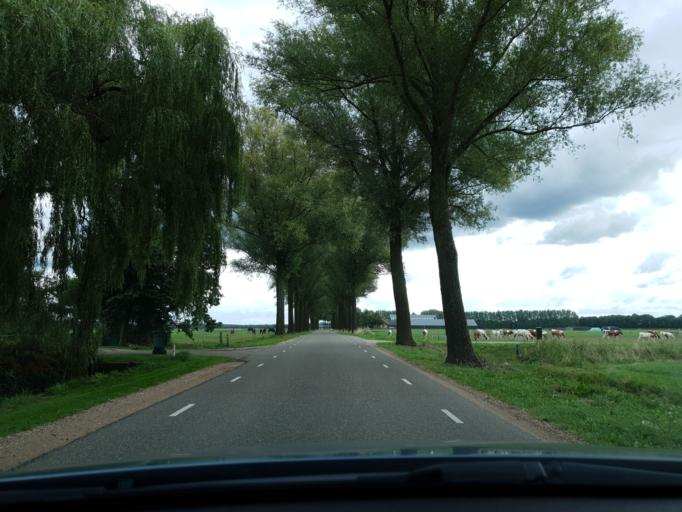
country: NL
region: Gelderland
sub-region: Gemeente Wijchen
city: Wijchen
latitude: 51.8436
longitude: 5.7129
